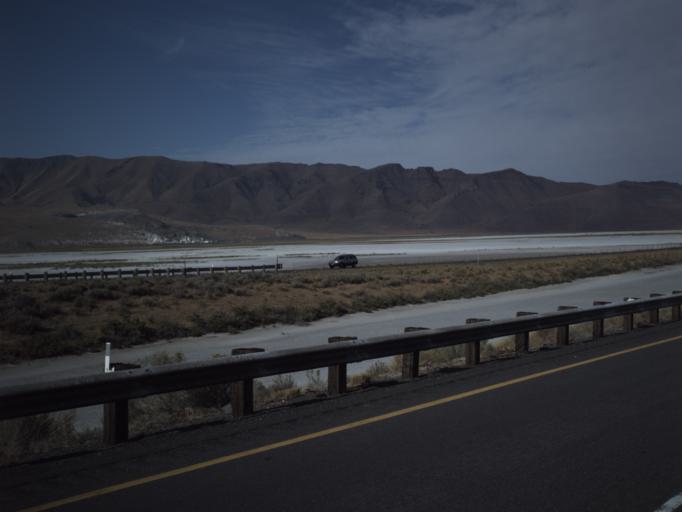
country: US
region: Utah
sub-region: Tooele County
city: Grantsville
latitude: 40.7111
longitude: -112.5326
